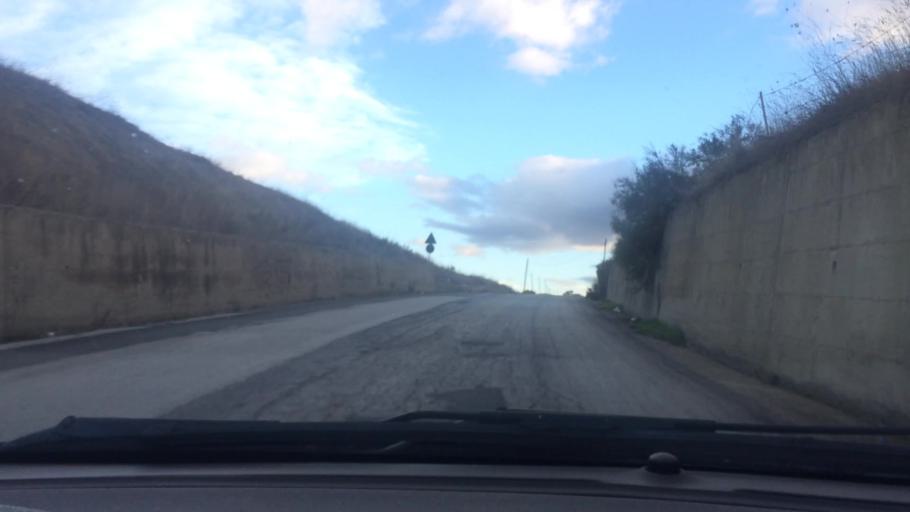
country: IT
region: Basilicate
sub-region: Provincia di Potenza
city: Tolve
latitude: 40.7068
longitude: 16.0161
